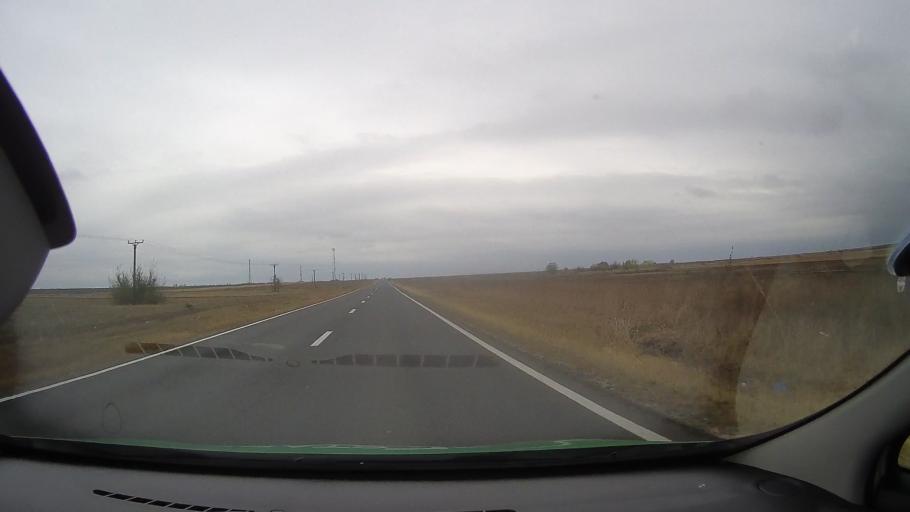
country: RO
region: Constanta
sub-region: Comuna Nicolae Balcescu
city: Nicolae Balcescu
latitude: 44.3764
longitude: 28.4203
